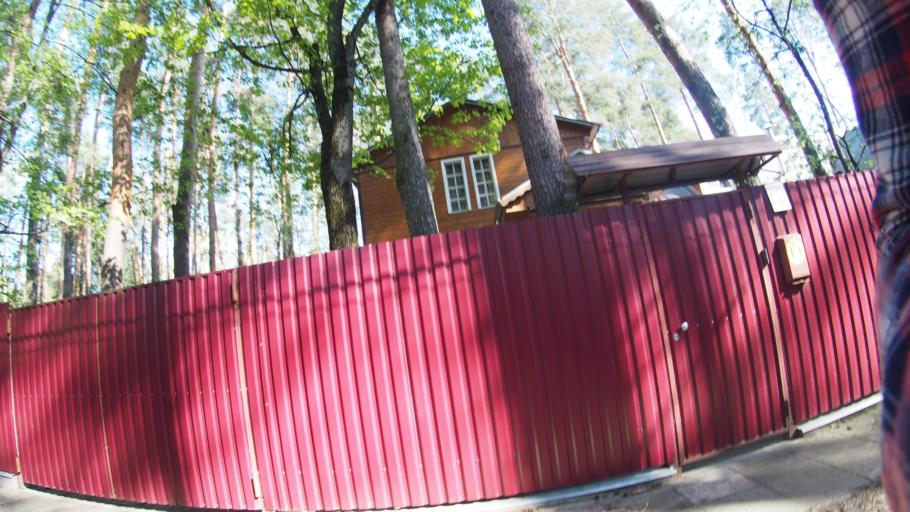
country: RU
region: Moskovskaya
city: Kratovo
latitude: 55.5872
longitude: 38.1824
